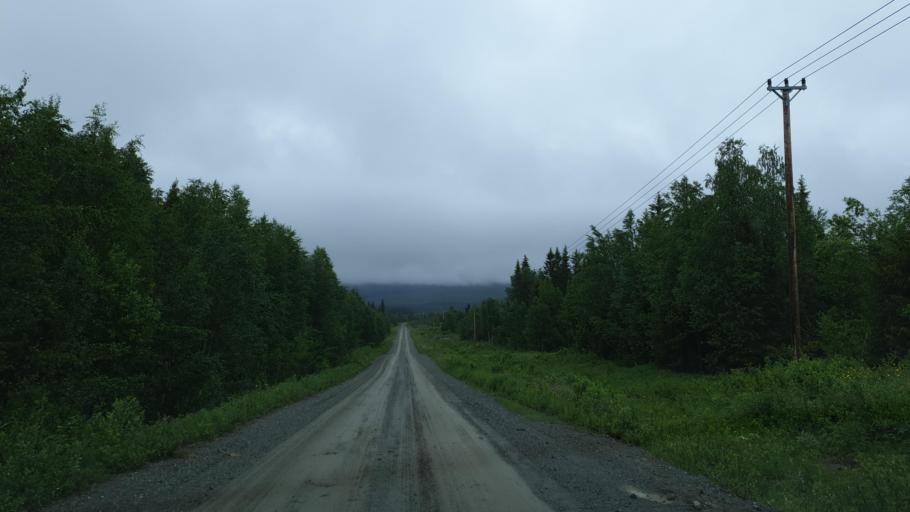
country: SE
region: Vaesterbotten
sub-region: Vilhelmina Kommun
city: Sjoberg
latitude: 65.3111
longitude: 16.0089
